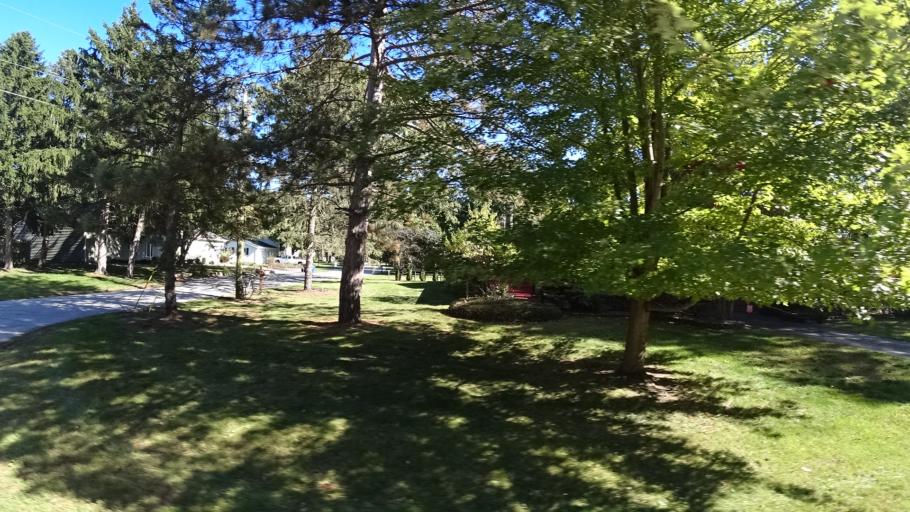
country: US
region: Indiana
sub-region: LaPorte County
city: Long Beach
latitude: 41.7489
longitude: -86.8352
